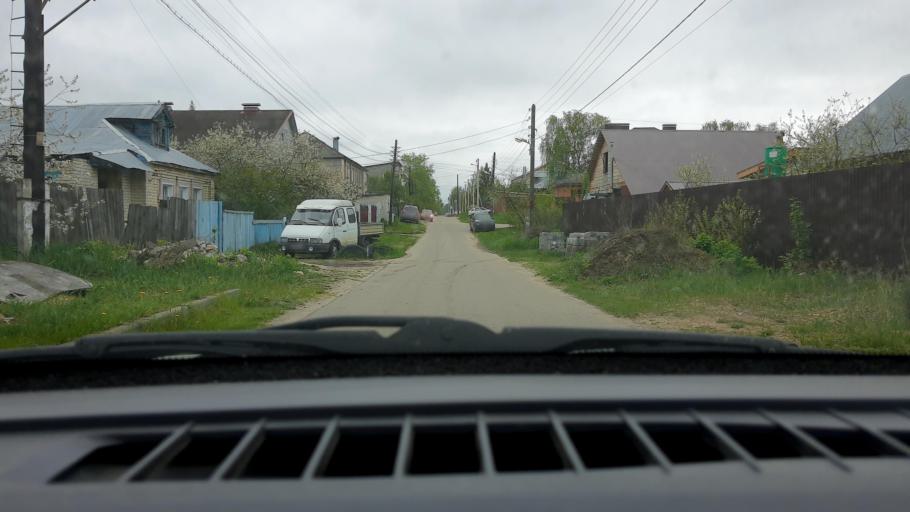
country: RU
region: Nizjnij Novgorod
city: Gorbatovka
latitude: 56.3370
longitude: 43.8259
